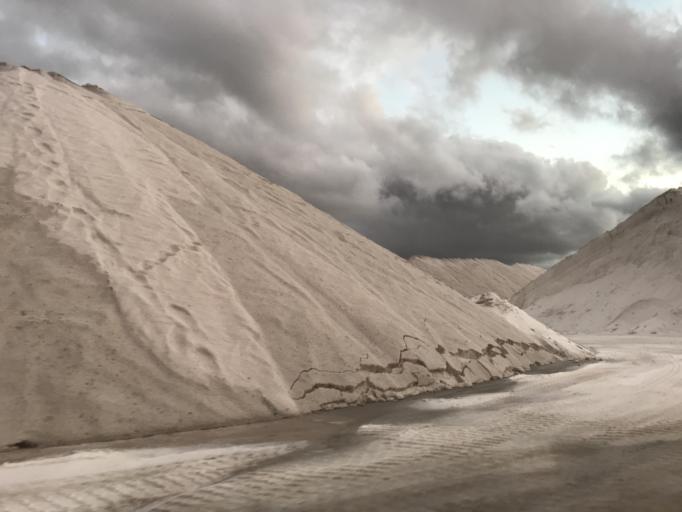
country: ES
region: Valencia
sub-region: Provincia de Alicante
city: Torrevieja
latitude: 37.9808
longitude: -0.6997
